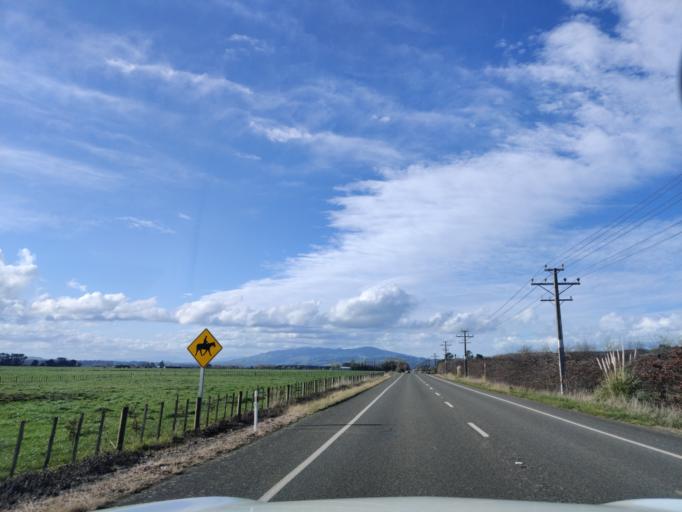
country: NZ
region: Manawatu-Wanganui
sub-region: Palmerston North City
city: Palmerston North
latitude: -40.3533
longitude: 175.6926
